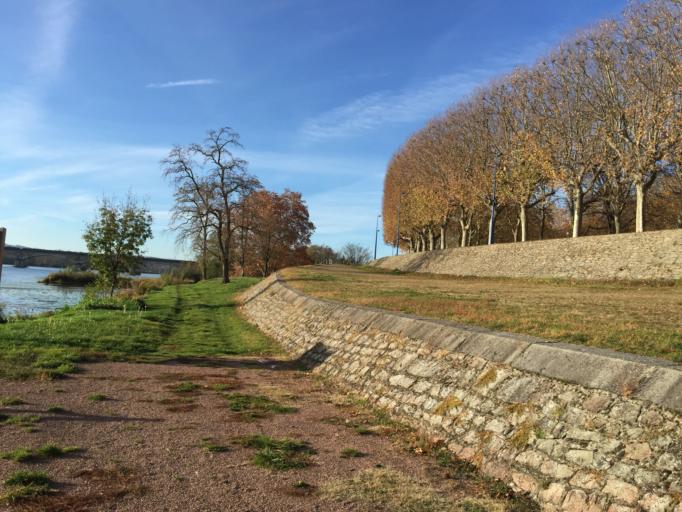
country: FR
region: Rhone-Alpes
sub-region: Departement de la Loire
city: Le Coteau
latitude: 46.0311
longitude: 4.0788
